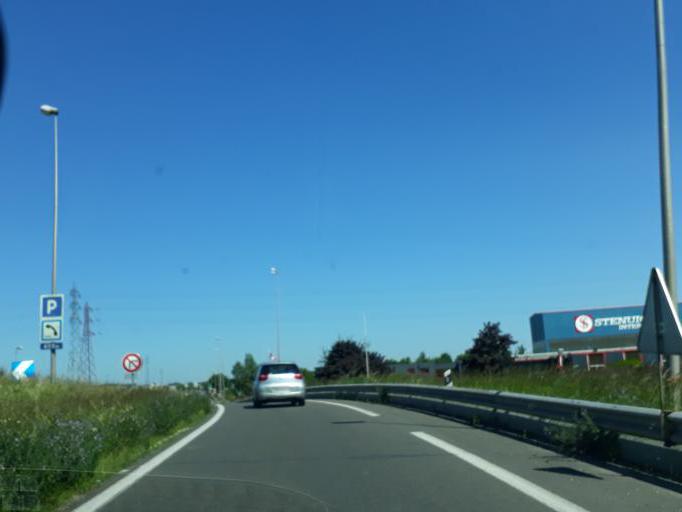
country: FR
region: Centre
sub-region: Departement du Loiret
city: Semoy
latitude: 47.9236
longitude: 1.9417
